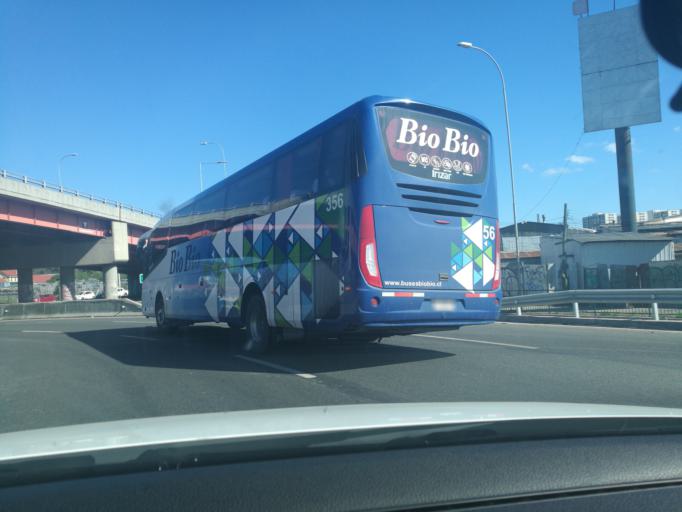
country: CL
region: Biobio
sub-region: Provincia de Concepcion
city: Concepcion
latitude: -36.8108
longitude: -73.0279
